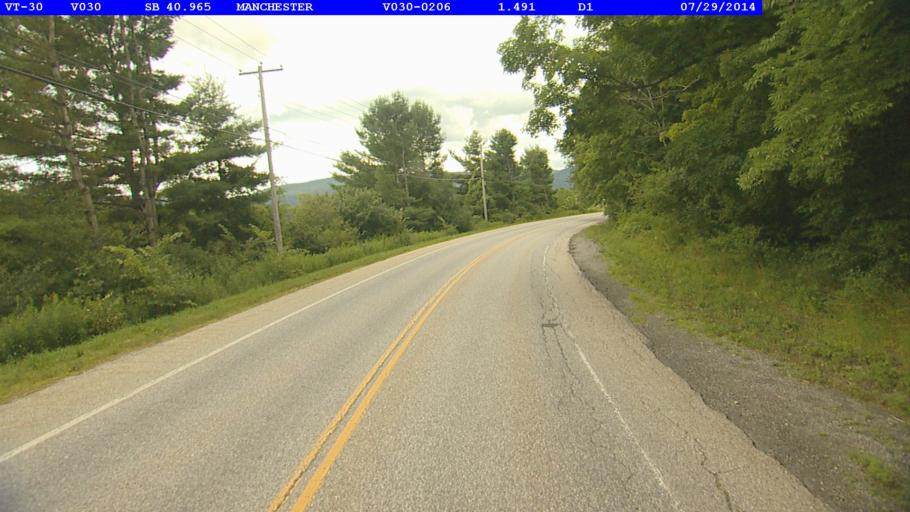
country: US
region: Vermont
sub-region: Bennington County
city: Manchester Center
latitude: 43.1975
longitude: -73.0531
